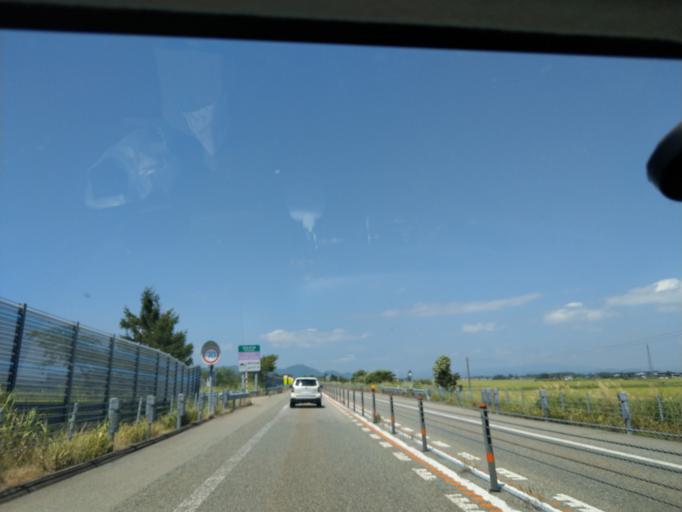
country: JP
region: Akita
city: Omagari
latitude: 39.3757
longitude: 140.4827
